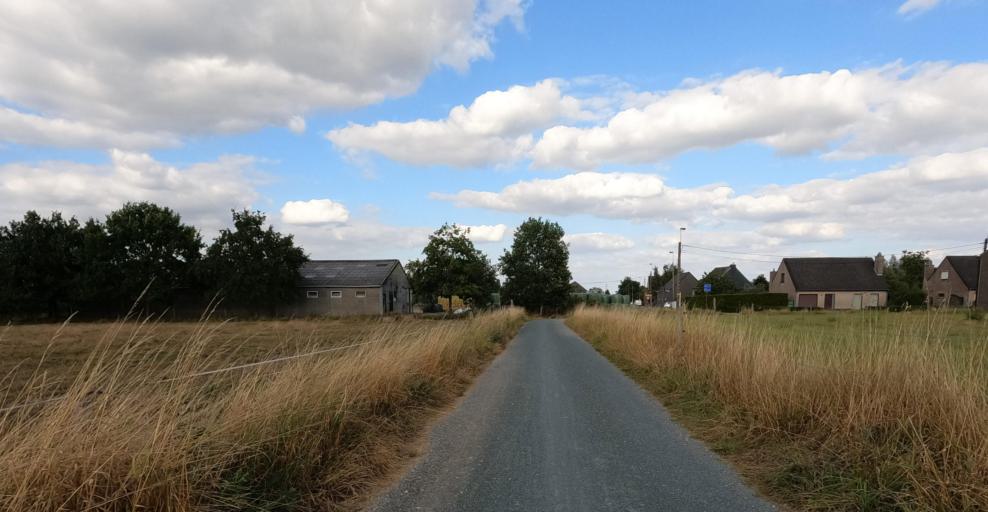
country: BE
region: Flanders
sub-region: Provincie Oost-Vlaanderen
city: Lebbeke
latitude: 51.0102
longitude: 4.1574
